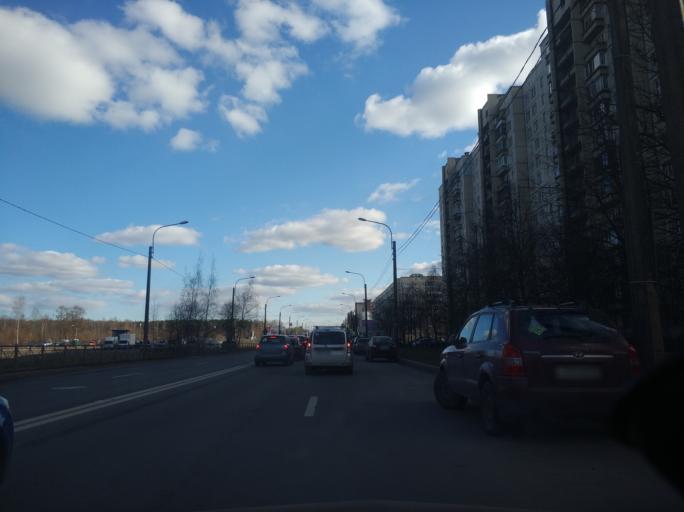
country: RU
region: St.-Petersburg
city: Krasnogvargeisky
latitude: 59.9548
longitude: 30.4959
